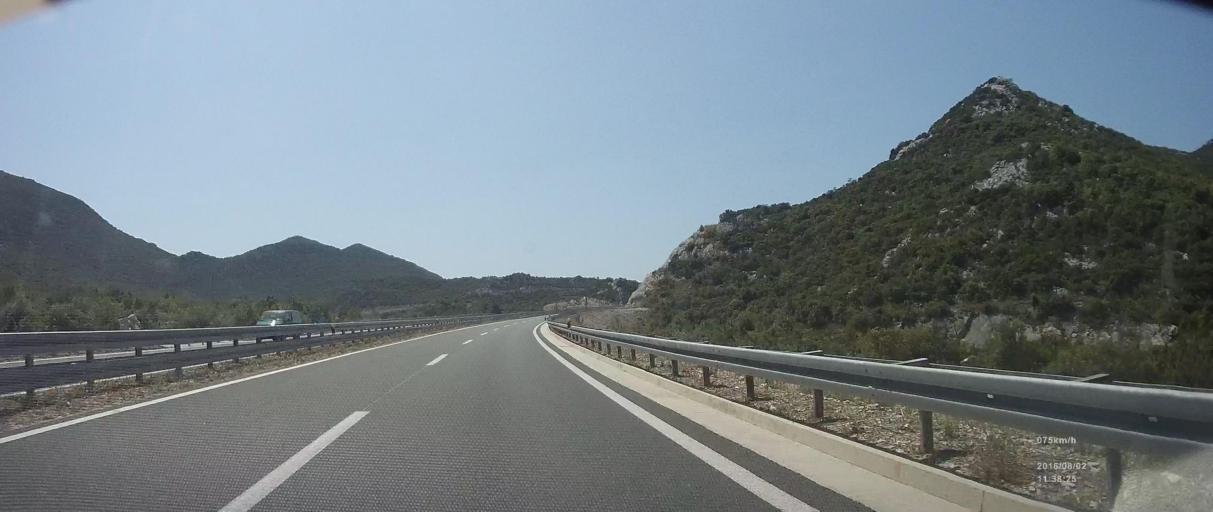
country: HR
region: Dubrovacko-Neretvanska
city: Komin
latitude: 43.0964
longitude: 17.4906
